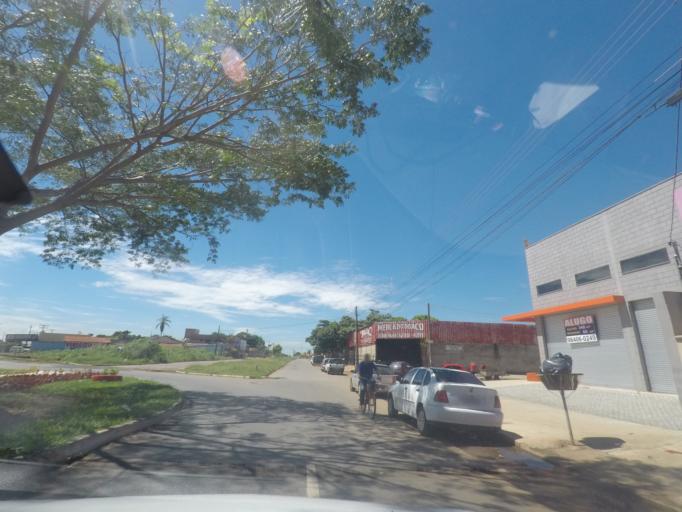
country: BR
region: Goias
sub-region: Aparecida De Goiania
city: Aparecida de Goiania
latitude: -16.7809
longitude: -49.3349
